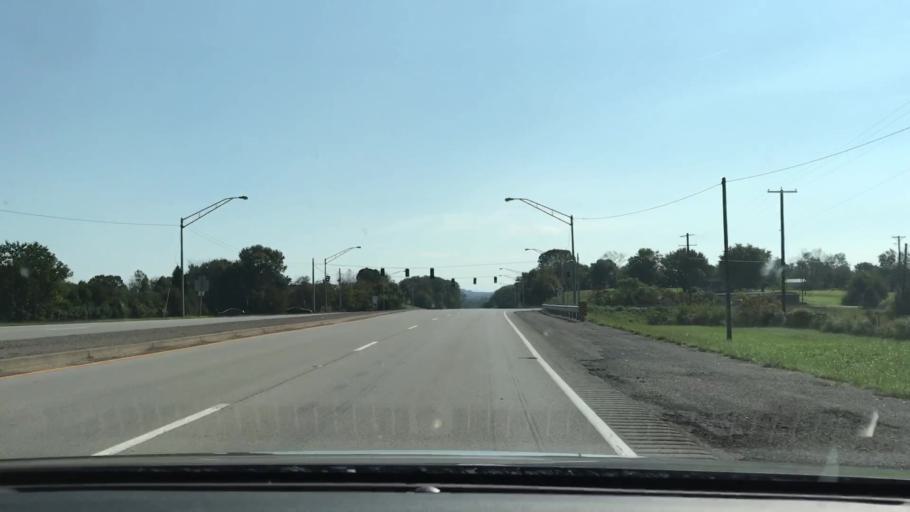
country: US
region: Kentucky
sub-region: Pulaski County
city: Somerset
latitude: 37.0935
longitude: -84.6318
